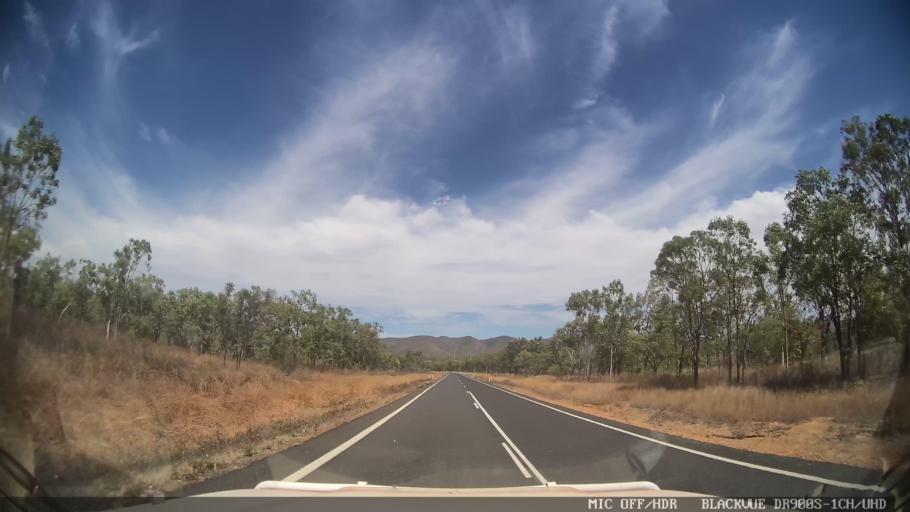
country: AU
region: Queensland
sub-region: Cook
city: Cooktown
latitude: -15.9325
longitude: 144.8402
